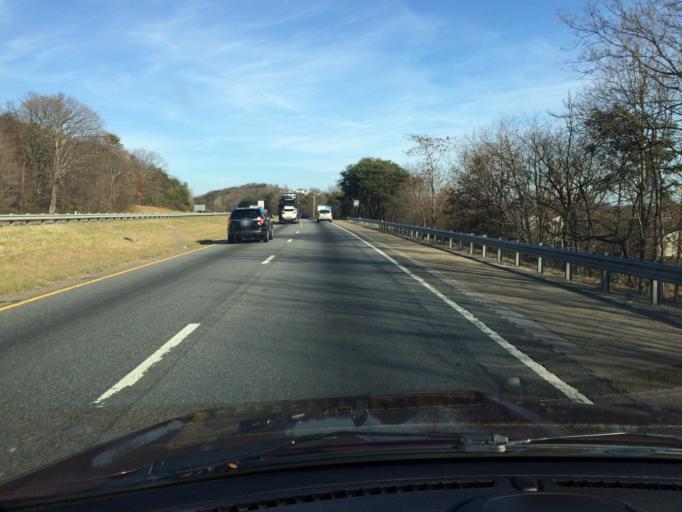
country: US
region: Virginia
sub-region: City of Salem
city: Salem
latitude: 37.2969
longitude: -80.0863
